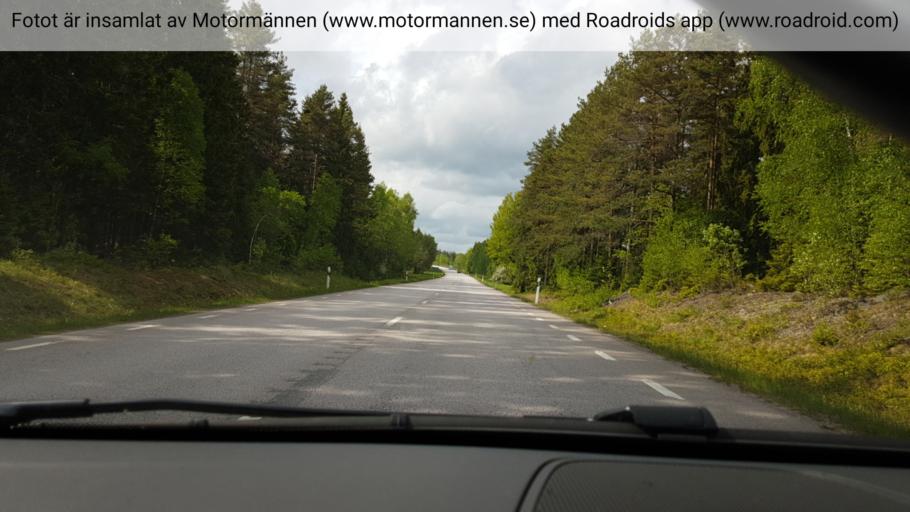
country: SE
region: Uppsala
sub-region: Tierps Kommun
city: Orbyhus
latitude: 60.2354
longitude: 17.6689
